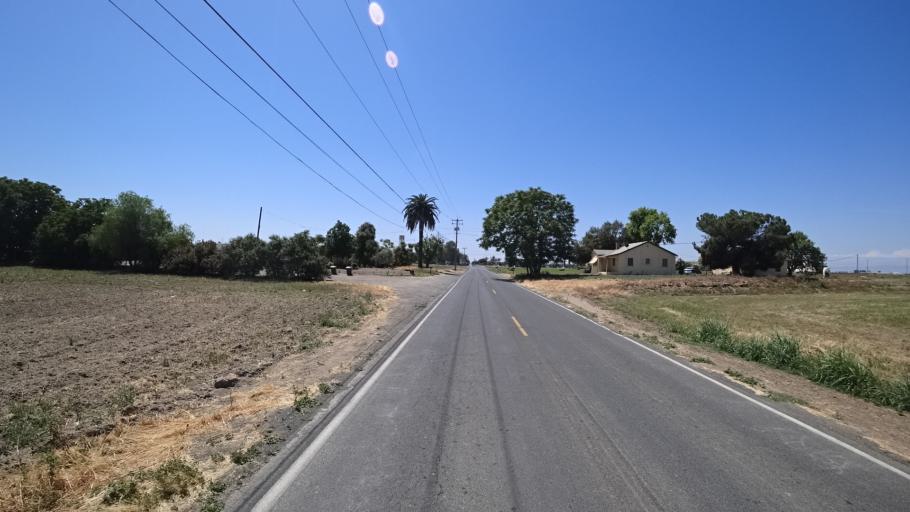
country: US
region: California
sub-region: Kings County
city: Lemoore
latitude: 36.2432
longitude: -119.7628
